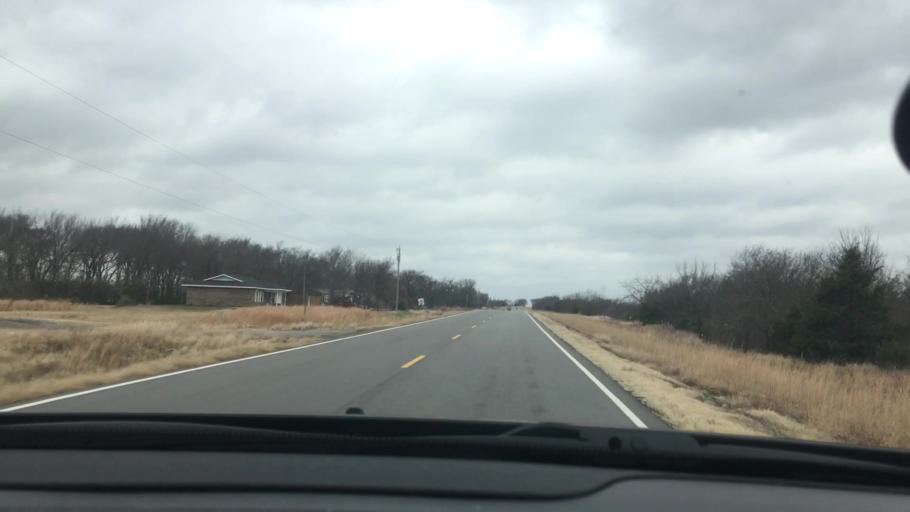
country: US
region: Oklahoma
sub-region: Atoka County
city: Atoka
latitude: 34.3747
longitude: -96.1833
